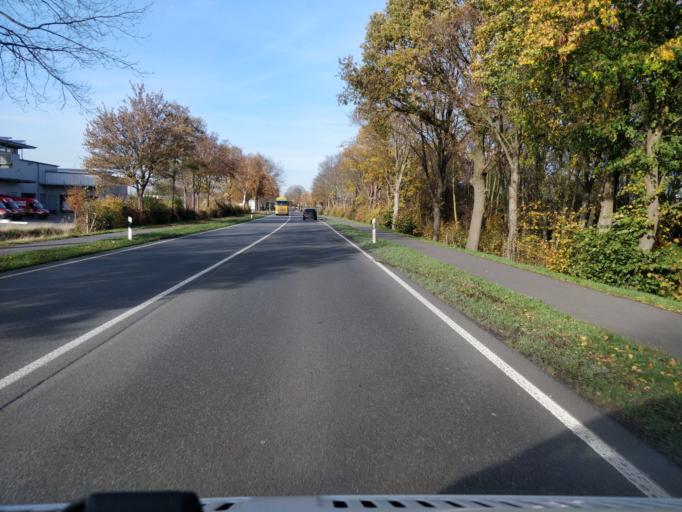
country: DE
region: North Rhine-Westphalia
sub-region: Regierungsbezirk Dusseldorf
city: Hamminkeln
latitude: 51.7394
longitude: 6.5968
